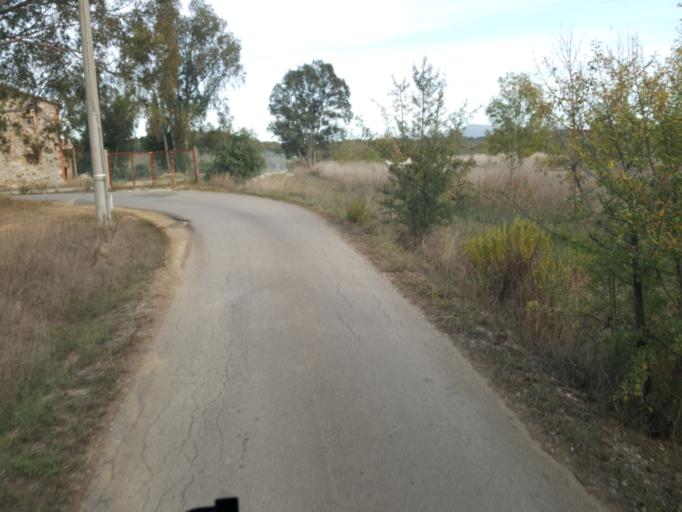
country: IT
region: Tuscany
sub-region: Provincia di Grosseto
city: Ribolla
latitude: 42.9472
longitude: 10.9949
